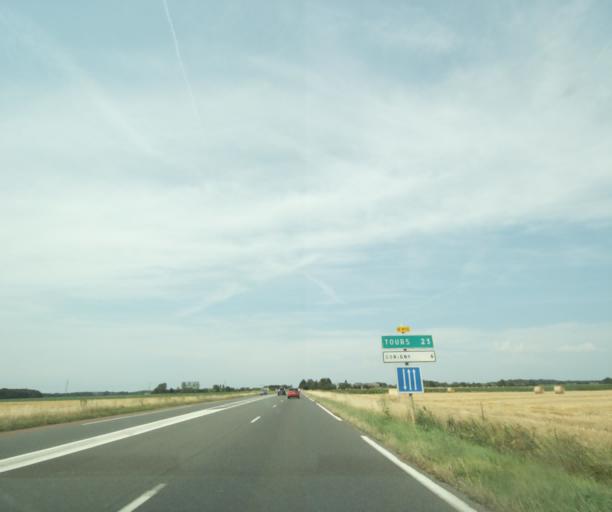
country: FR
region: Centre
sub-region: Departement d'Indre-et-Loire
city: Sorigny
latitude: 47.2012
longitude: 0.6712
